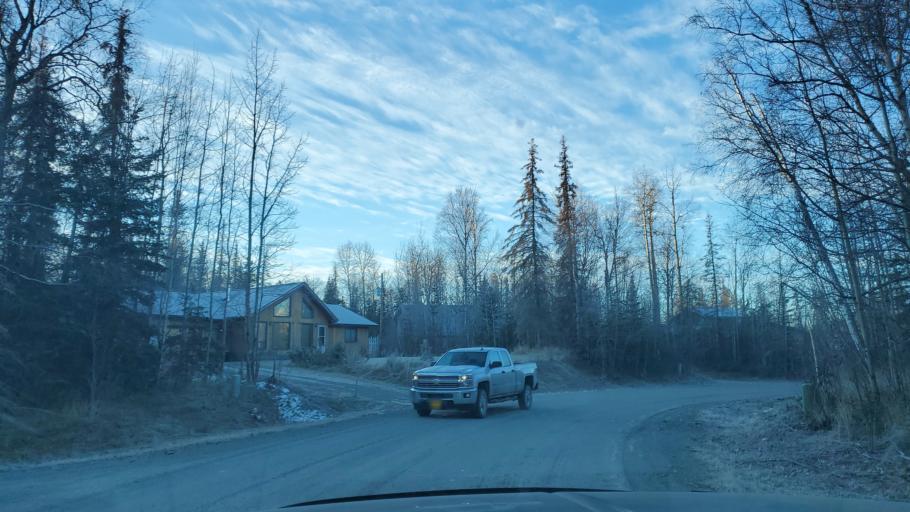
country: US
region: Alaska
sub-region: Matanuska-Susitna Borough
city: Tanaina
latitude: 61.6075
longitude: -149.4025
